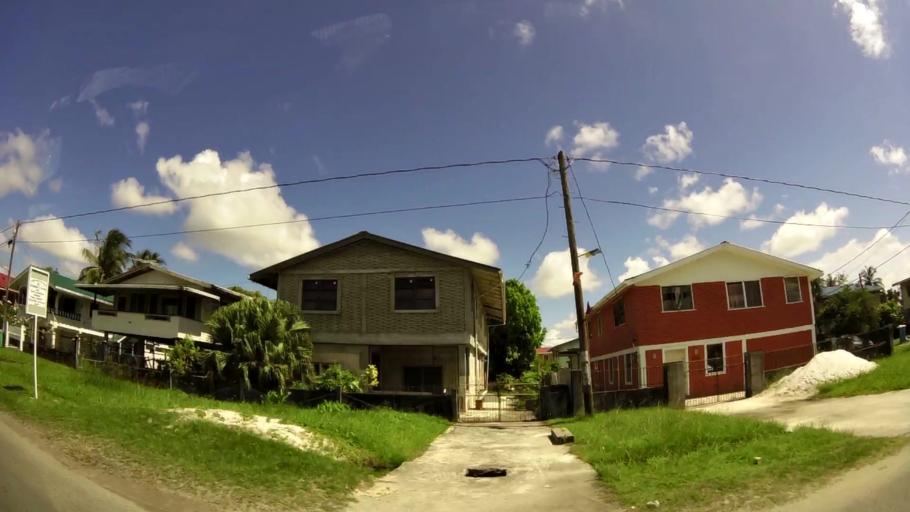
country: GY
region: Demerara-Mahaica
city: Georgetown
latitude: 6.7832
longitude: -58.1288
